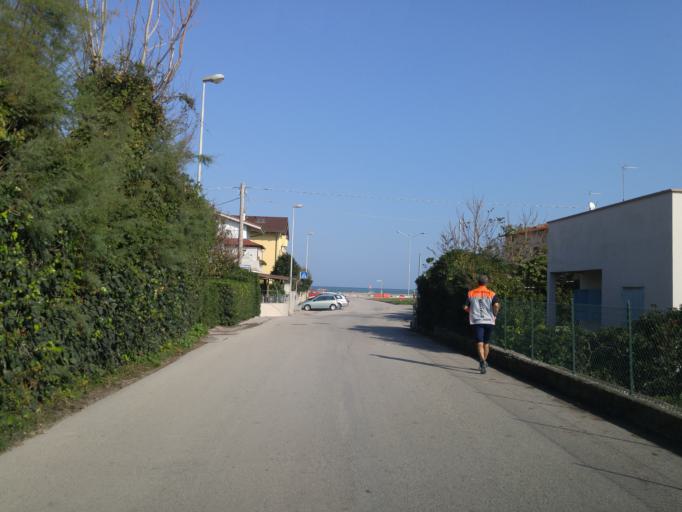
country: IT
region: The Marches
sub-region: Provincia di Pesaro e Urbino
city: Fano
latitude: 43.8398
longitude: 13.0339
